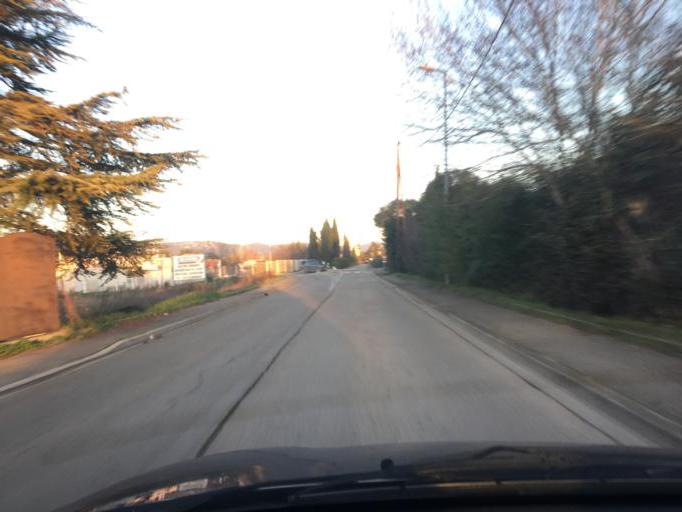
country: FR
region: Provence-Alpes-Cote d'Azur
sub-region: Departement des Bouches-du-Rhone
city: Mallemort
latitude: 43.7299
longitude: 5.1669
